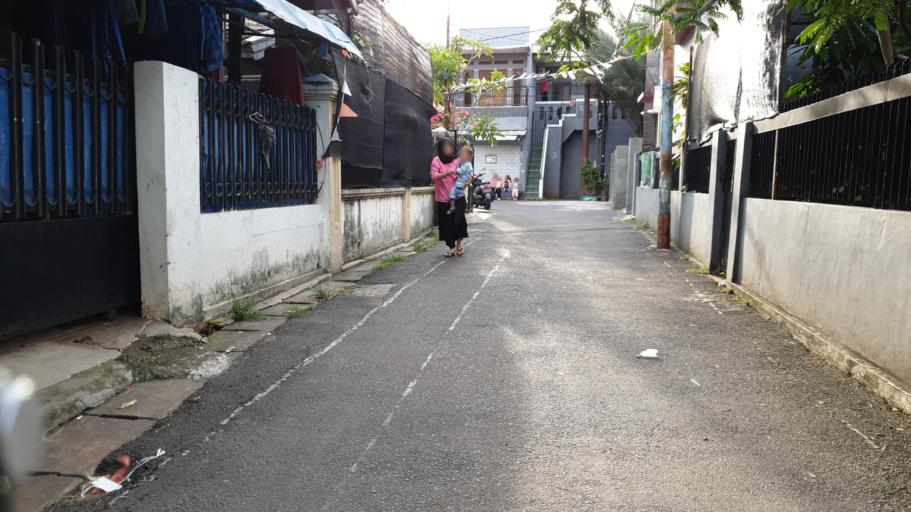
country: ID
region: Banten
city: South Tangerang
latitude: -6.2862
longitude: 106.7894
